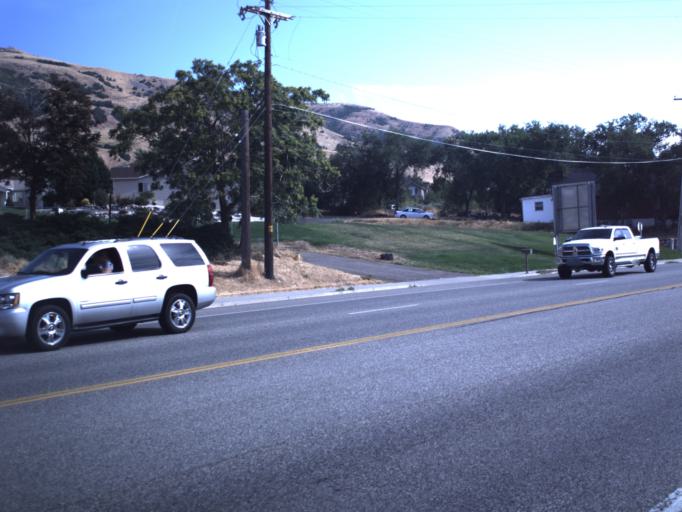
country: US
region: Utah
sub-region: Box Elder County
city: Perry
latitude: 41.4845
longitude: -112.0173
